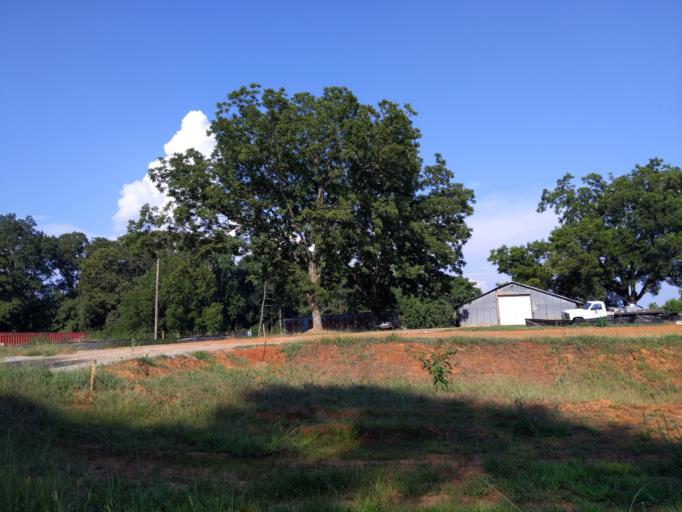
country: US
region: Georgia
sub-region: Hall County
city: Flowery Branch
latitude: 34.1404
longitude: -83.8830
